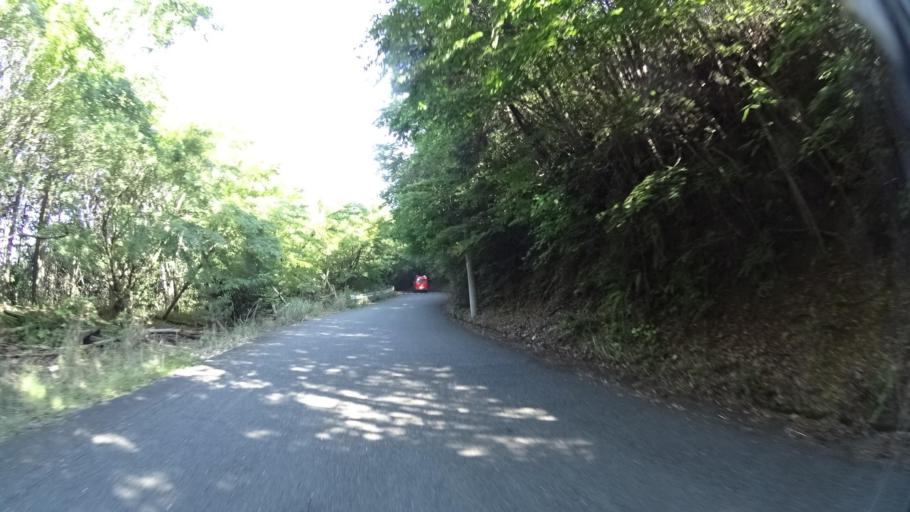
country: JP
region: Kyoto
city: Kameoka
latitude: 34.9989
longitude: 135.5606
